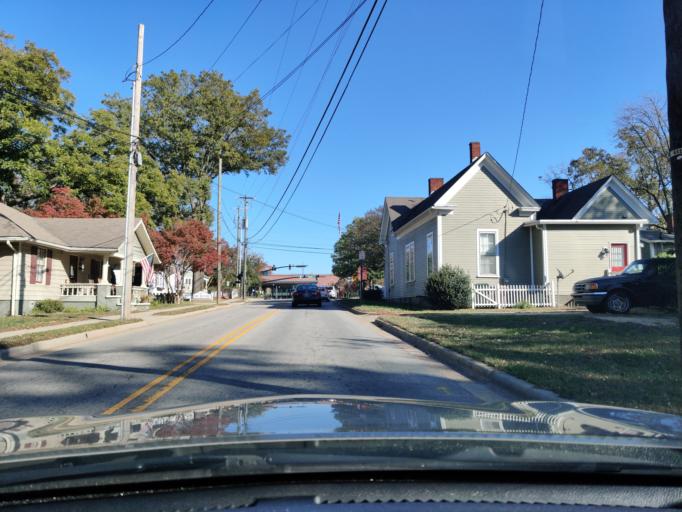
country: US
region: North Carolina
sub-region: Wake County
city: Cary
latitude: 35.7831
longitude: -78.7825
